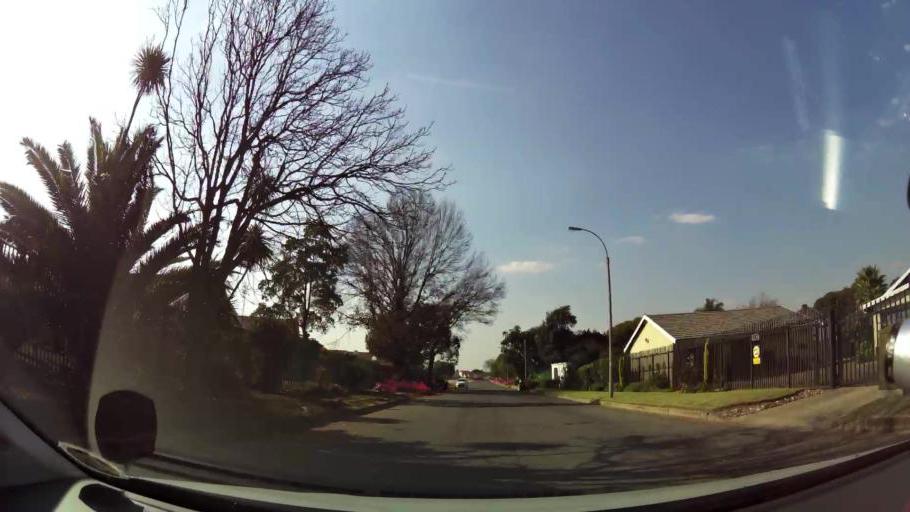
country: ZA
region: Gauteng
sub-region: City of Johannesburg Metropolitan Municipality
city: Modderfontein
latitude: -26.0939
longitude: 28.2026
